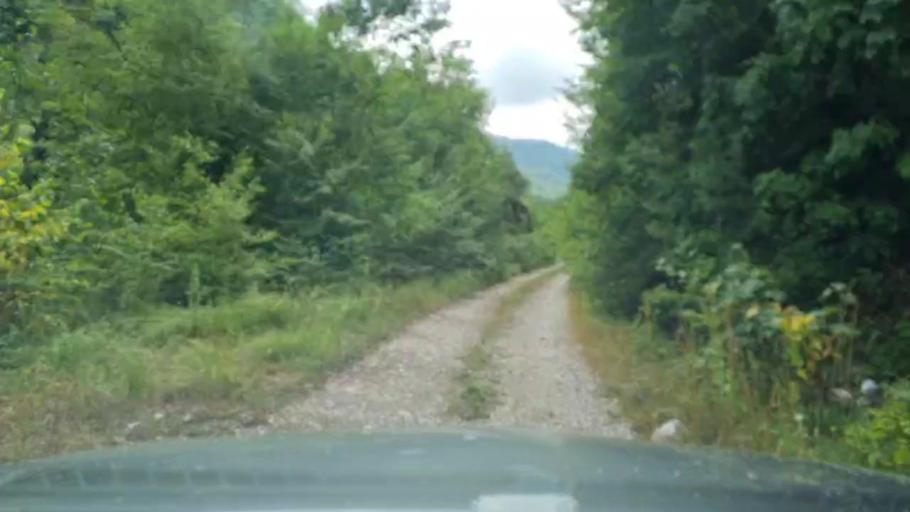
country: BA
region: Republika Srpska
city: Rogatica
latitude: 43.7663
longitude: 18.8736
